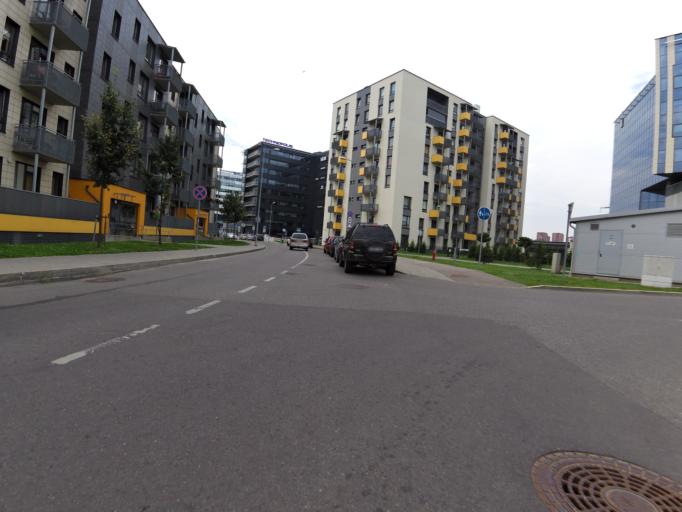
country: LT
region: Vilnius County
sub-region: Vilnius
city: Vilnius
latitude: 54.7208
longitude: 25.2839
